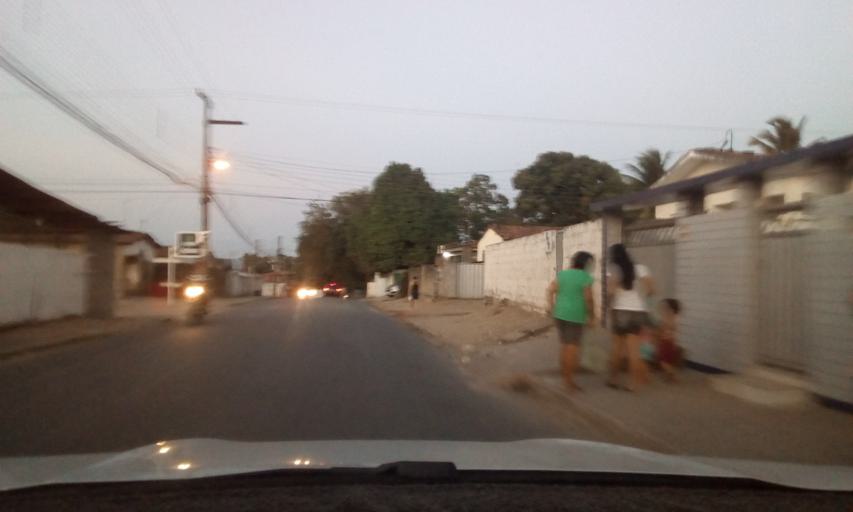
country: BR
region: Paraiba
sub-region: Bayeux
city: Bayeux
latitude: -7.1690
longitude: -34.9108
